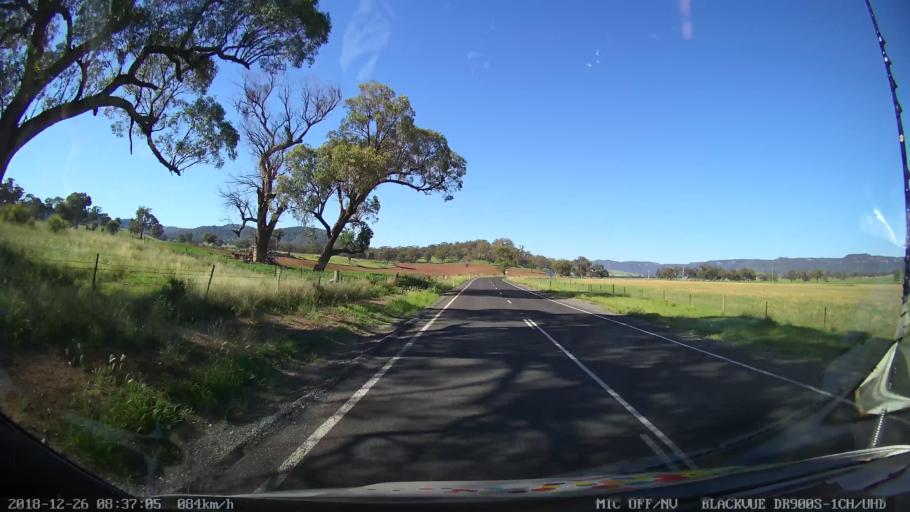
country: AU
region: New South Wales
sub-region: Upper Hunter Shire
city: Merriwa
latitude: -32.4288
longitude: 150.0932
